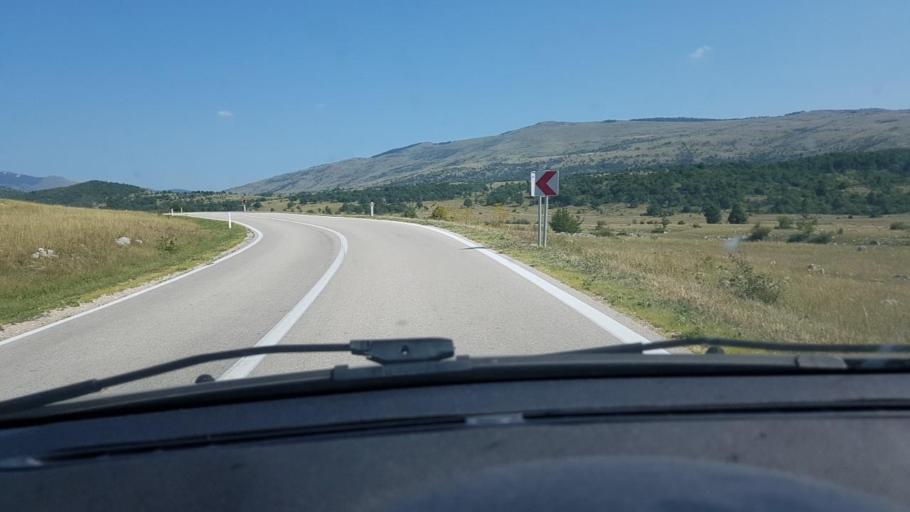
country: BA
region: Federation of Bosnia and Herzegovina
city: Bosansko Grahovo
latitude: 44.1345
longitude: 16.4764
